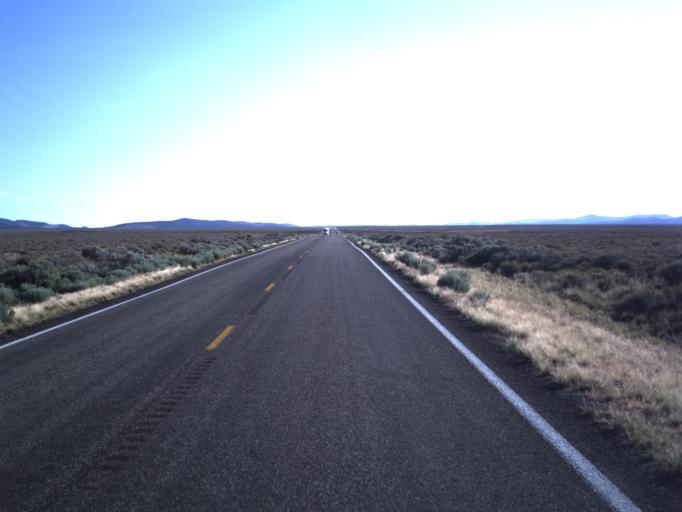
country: US
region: Utah
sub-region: Iron County
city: Enoch
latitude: 37.9319
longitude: -113.0280
